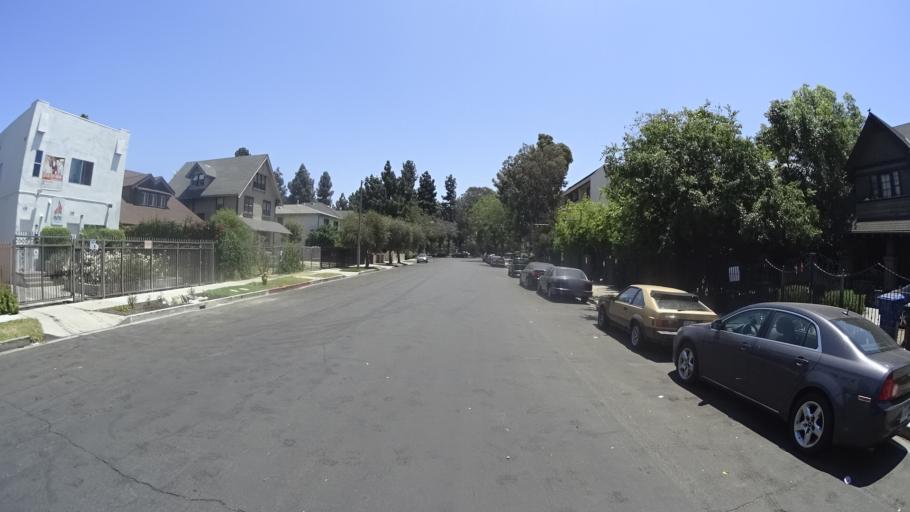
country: US
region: California
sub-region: Los Angeles County
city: Los Angeles
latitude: 34.0210
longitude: -118.2934
